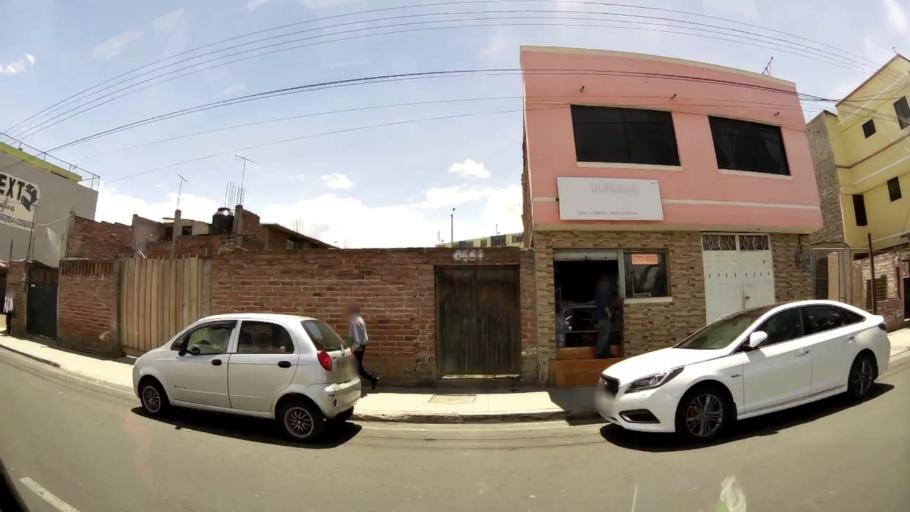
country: EC
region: Chimborazo
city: Riobamba
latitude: -1.6806
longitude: -78.6399
